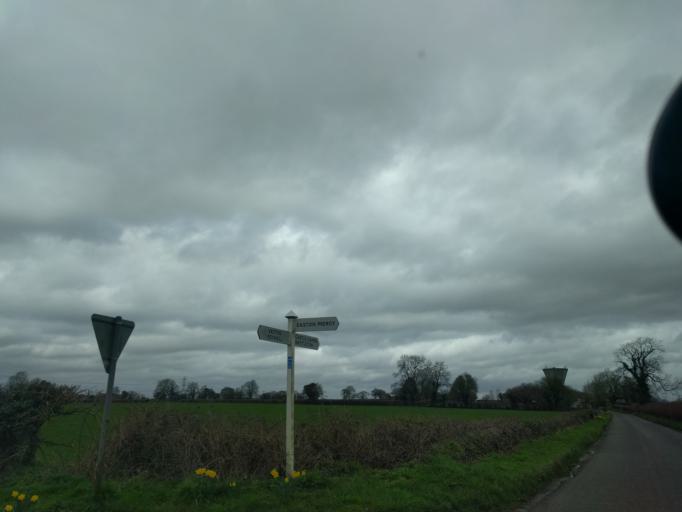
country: GB
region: England
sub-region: Wiltshire
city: Biddestone
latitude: 51.4937
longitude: -2.1926
